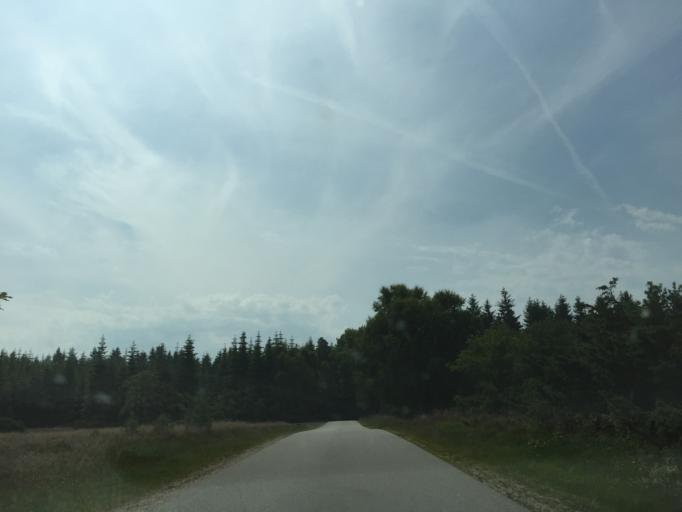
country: DK
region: Central Jutland
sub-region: Silkeborg Kommune
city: Virklund
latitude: 56.0740
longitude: 9.4707
